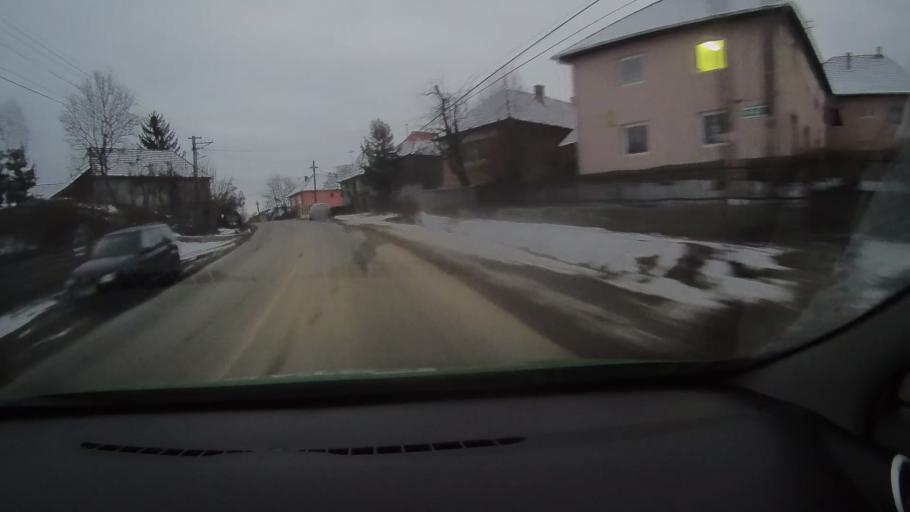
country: RO
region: Harghita
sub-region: Comuna Darjiu
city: Darjiu
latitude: 46.2123
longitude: 25.2398
